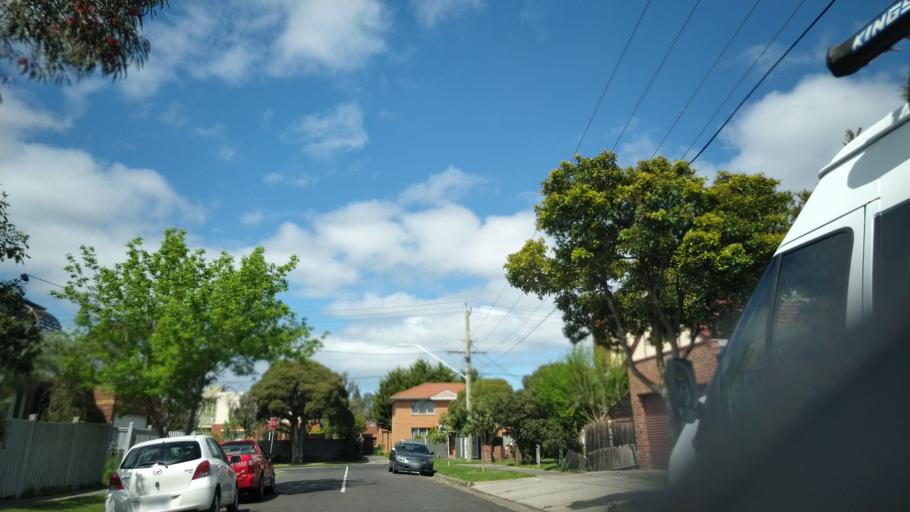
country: AU
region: Victoria
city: Murrumbeena
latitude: -37.8993
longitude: 145.0582
